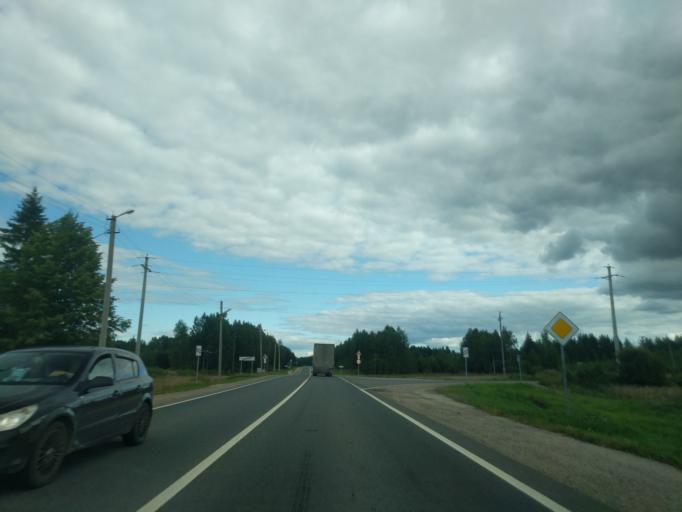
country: RU
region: Kostroma
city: Ostrovskoye
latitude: 57.8200
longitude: 42.2002
